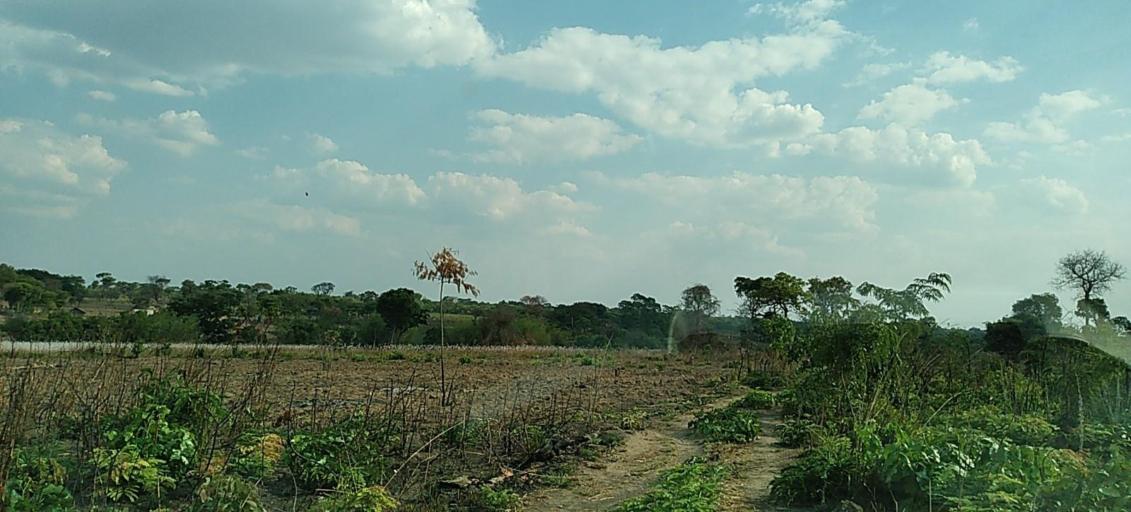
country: ZM
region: Copperbelt
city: Chililabombwe
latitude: -12.3568
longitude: 27.3962
